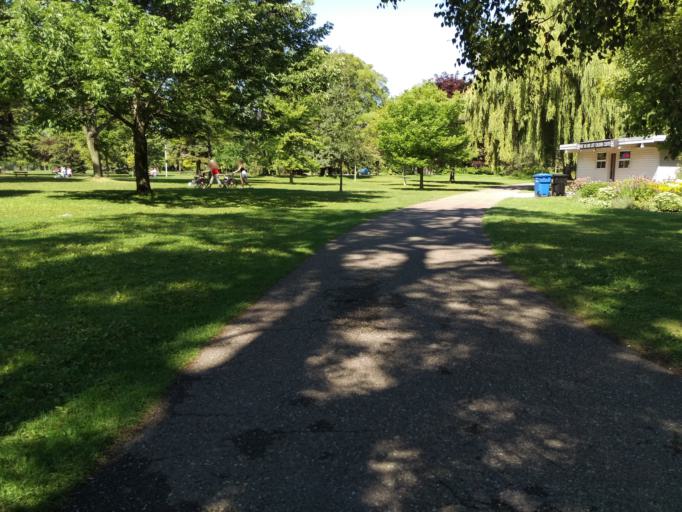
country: CA
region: Ontario
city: Toronto
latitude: 43.6212
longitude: -79.3762
